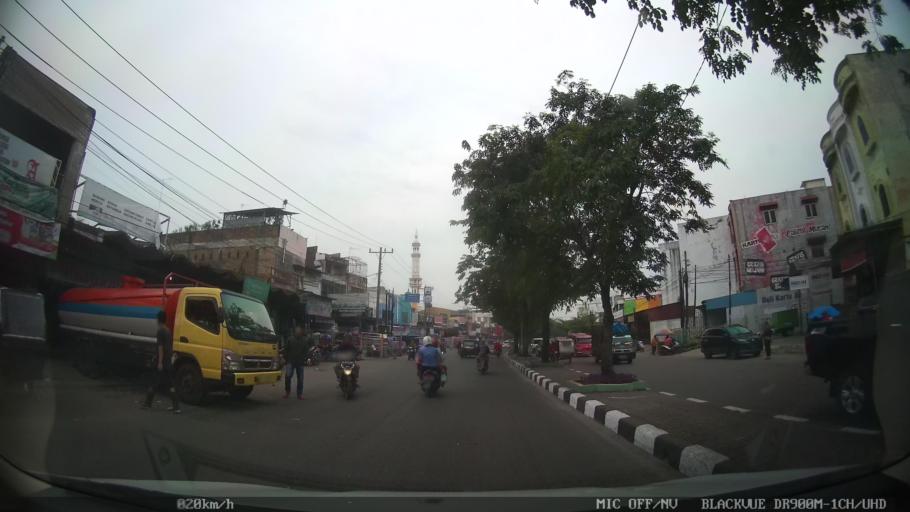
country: ID
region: North Sumatra
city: Medan
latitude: 3.5522
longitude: 98.6972
